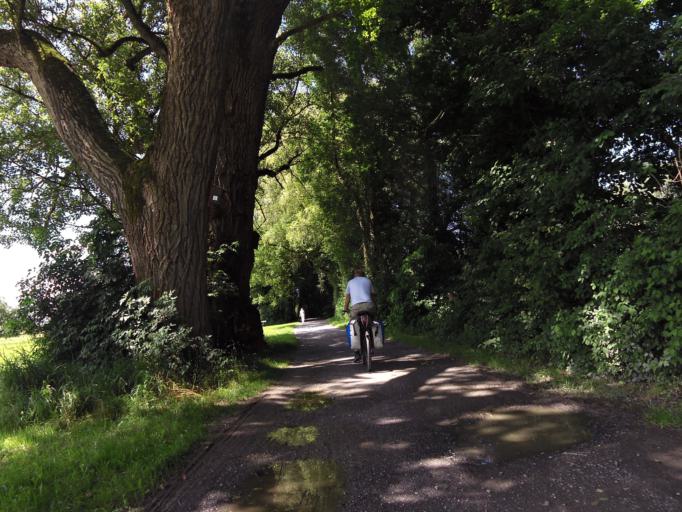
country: CH
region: Saint Gallen
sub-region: Wahlkreis Rheintal
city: Rheineck
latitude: 47.4840
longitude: 9.5783
